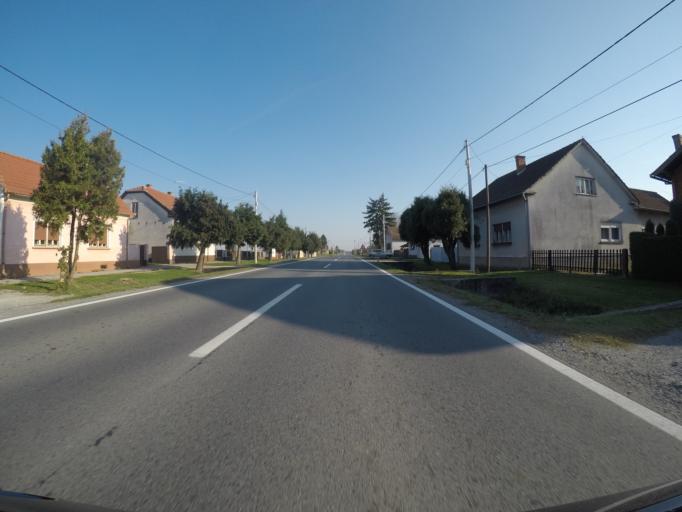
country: HR
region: Koprivnicko-Krizevacka
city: Kalinovac
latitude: 45.9802
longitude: 17.1632
